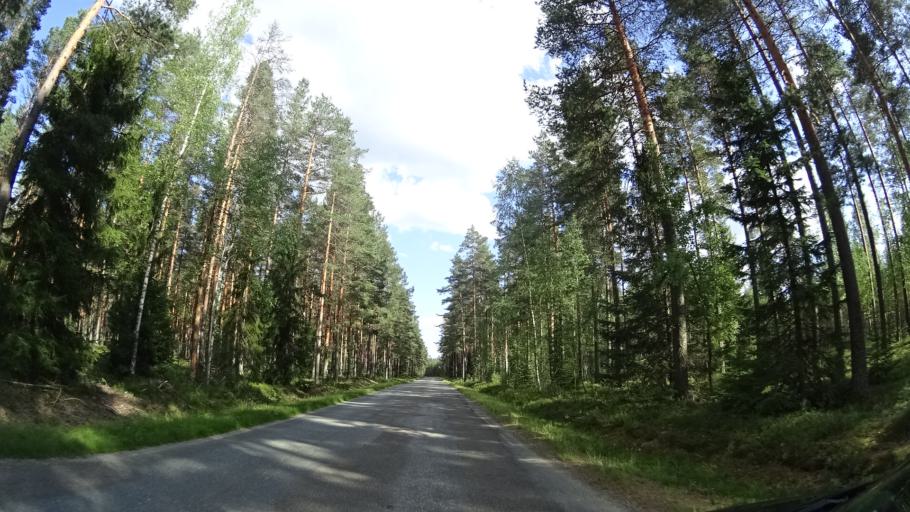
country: FI
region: Uusimaa
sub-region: Helsinki
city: Kaerkoelae
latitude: 60.7421
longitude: 24.0853
